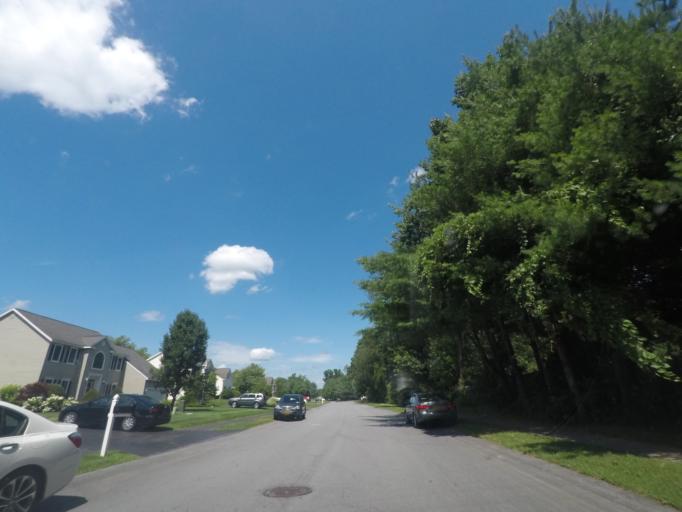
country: US
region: New York
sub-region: Schenectady County
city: Rotterdam
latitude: 42.7446
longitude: -73.9314
